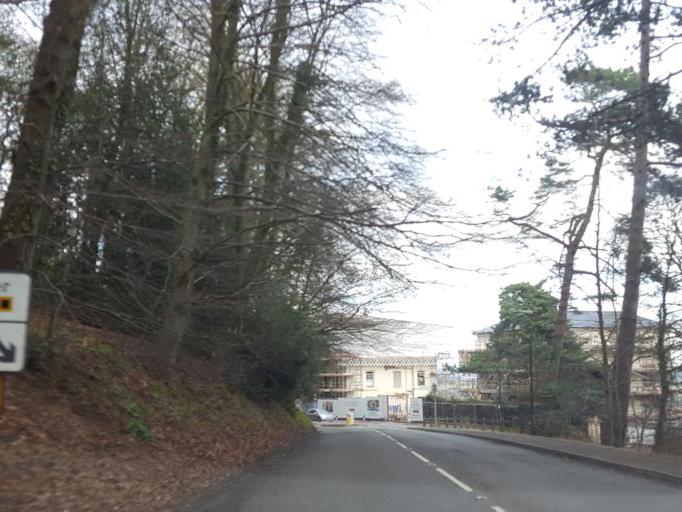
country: GB
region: England
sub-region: Worcestershire
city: Great Malvern
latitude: 52.1047
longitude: -2.3303
